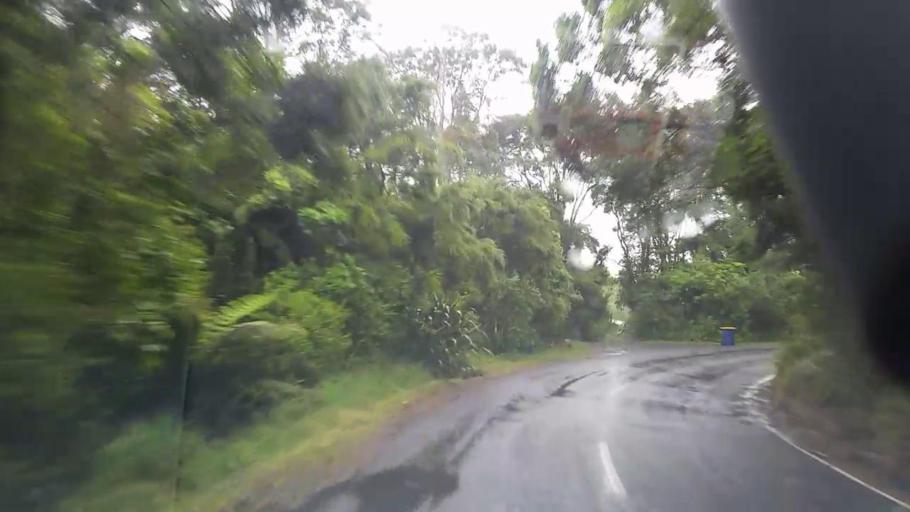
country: NZ
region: Auckland
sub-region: Auckland
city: Waitakere
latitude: -36.9046
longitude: 174.5712
